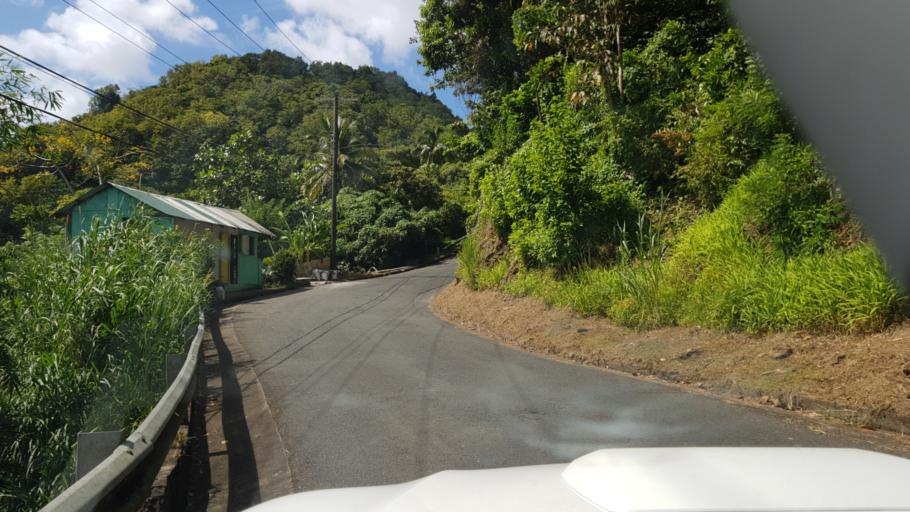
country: LC
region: Castries Quarter
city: Castries
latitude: 13.9895
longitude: -60.9729
